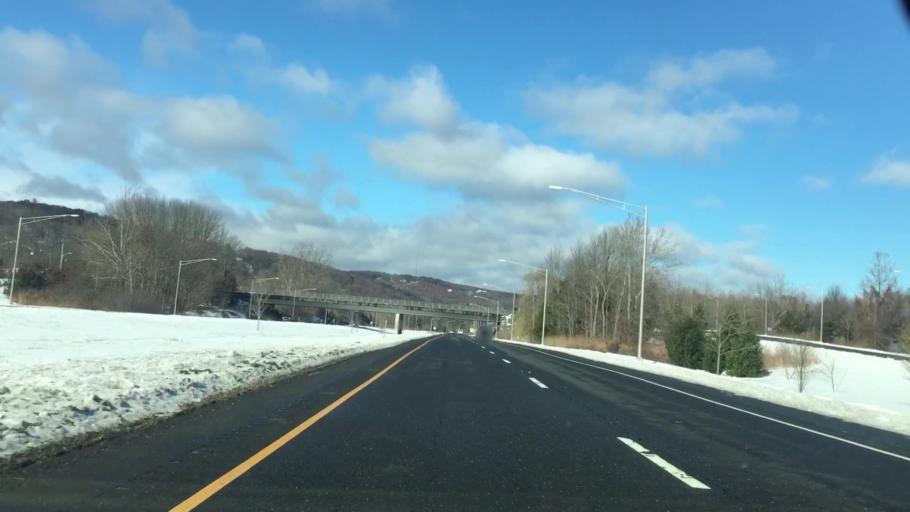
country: US
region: Connecticut
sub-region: Fairfield County
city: Danbury
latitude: 41.4702
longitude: -73.4062
